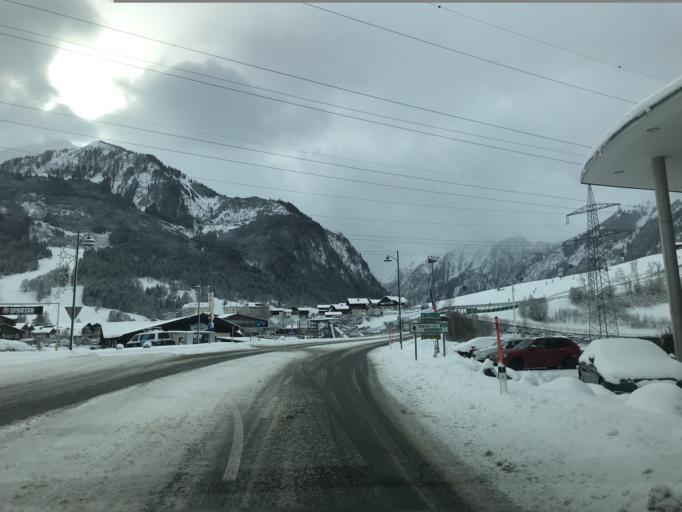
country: AT
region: Salzburg
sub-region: Politischer Bezirk Zell am See
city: Kaprun
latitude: 47.2766
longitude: 12.7575
